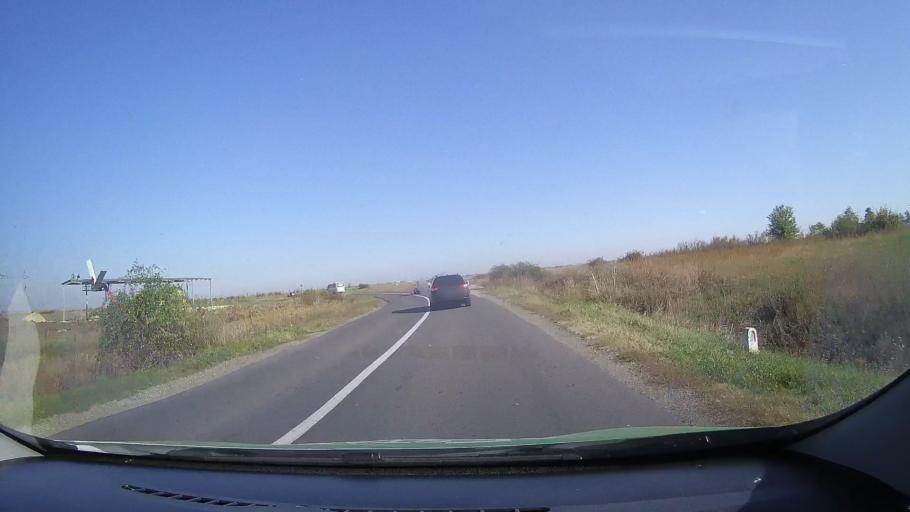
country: RO
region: Satu Mare
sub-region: Comuna Cauas
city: Cauas
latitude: 47.5749
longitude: 22.5496
